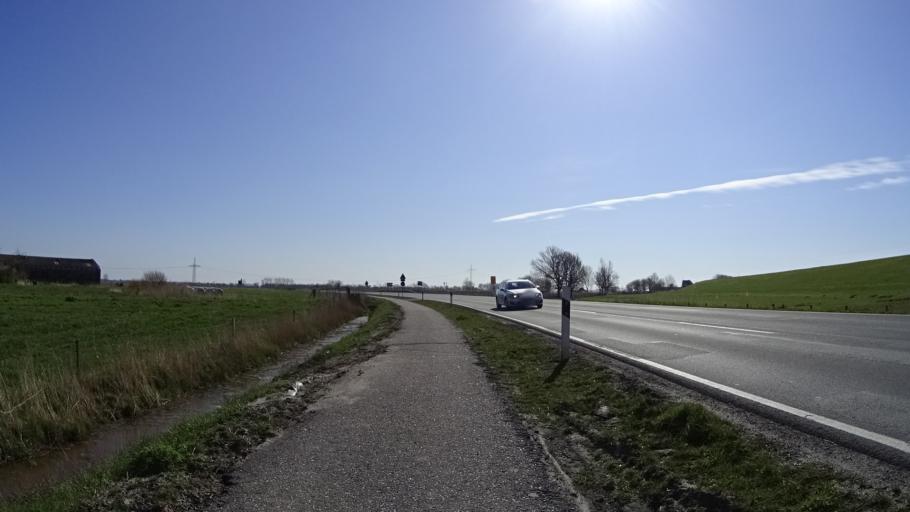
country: DE
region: Lower Saxony
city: Jemgum
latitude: 53.2959
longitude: 7.3946
